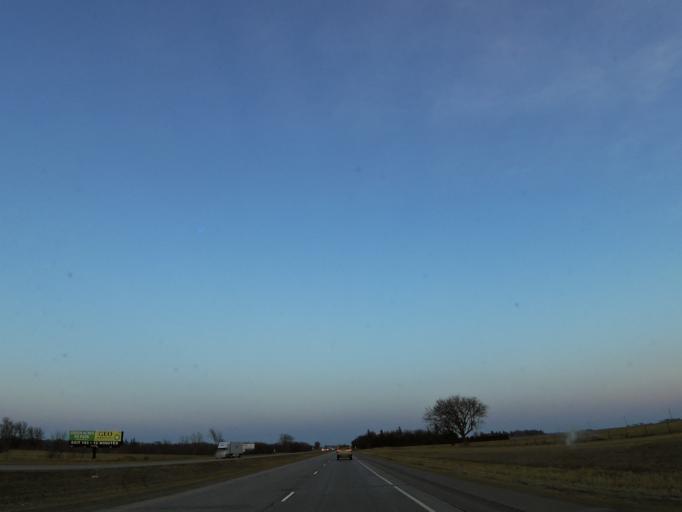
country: US
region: Minnesota
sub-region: Mower County
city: Austin
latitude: 43.6714
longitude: -92.8885
